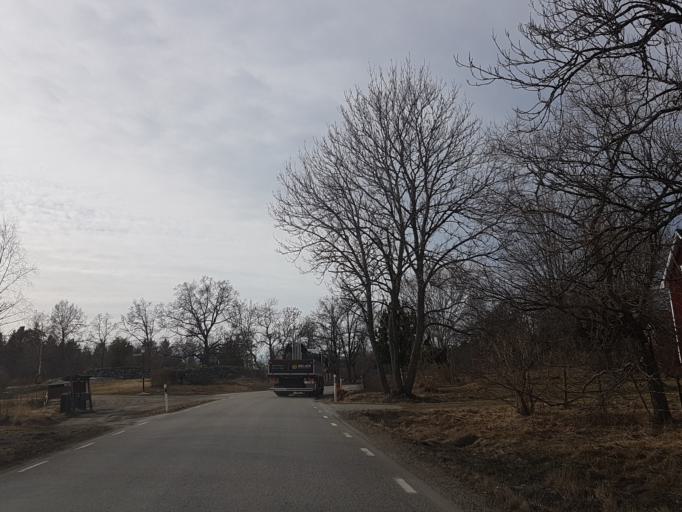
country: SE
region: Stockholm
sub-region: Norrtalje Kommun
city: Bjorko
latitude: 59.6648
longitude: 18.8843
